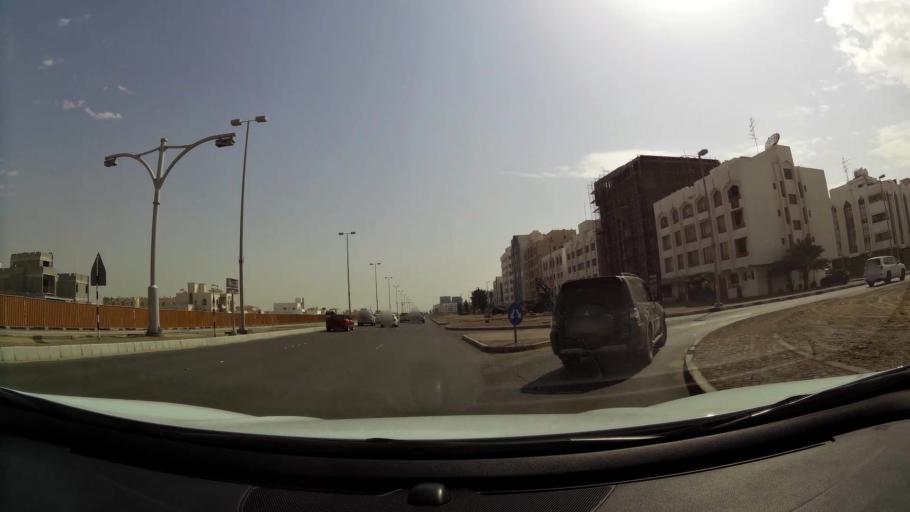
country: AE
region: Abu Dhabi
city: Abu Dhabi
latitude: 24.3361
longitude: 54.5384
